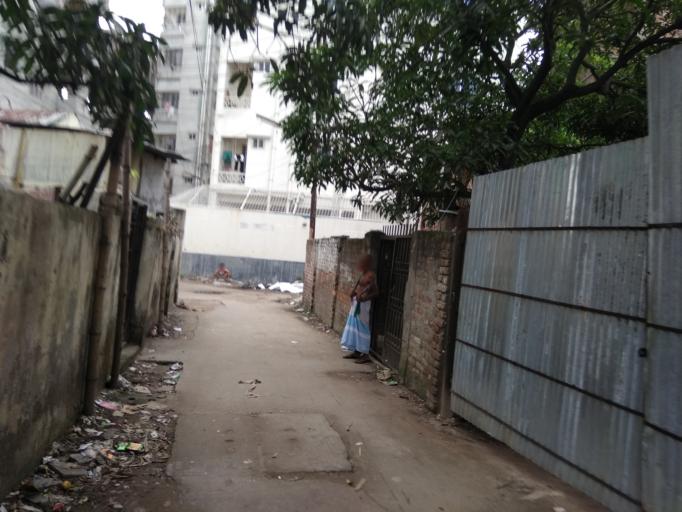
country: BD
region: Dhaka
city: Azimpur
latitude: 23.7981
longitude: 90.3772
